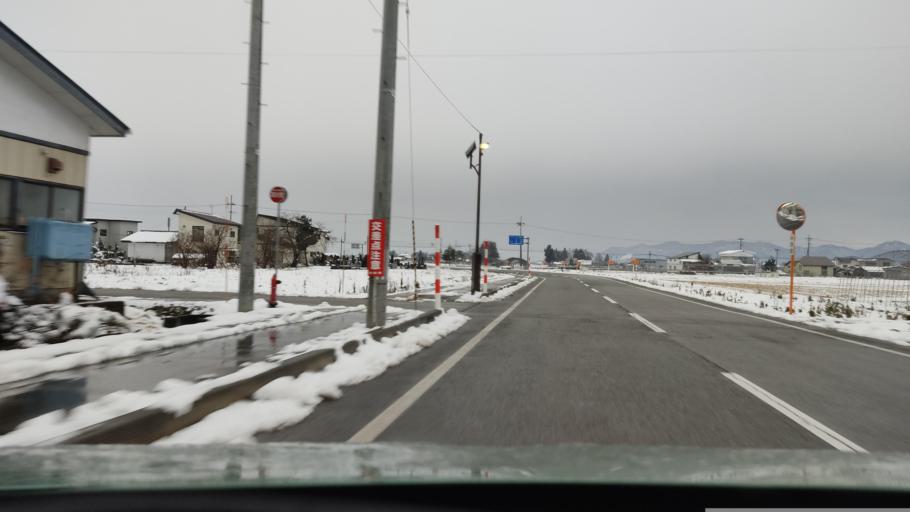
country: JP
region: Akita
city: Omagari
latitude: 39.4297
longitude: 140.5272
